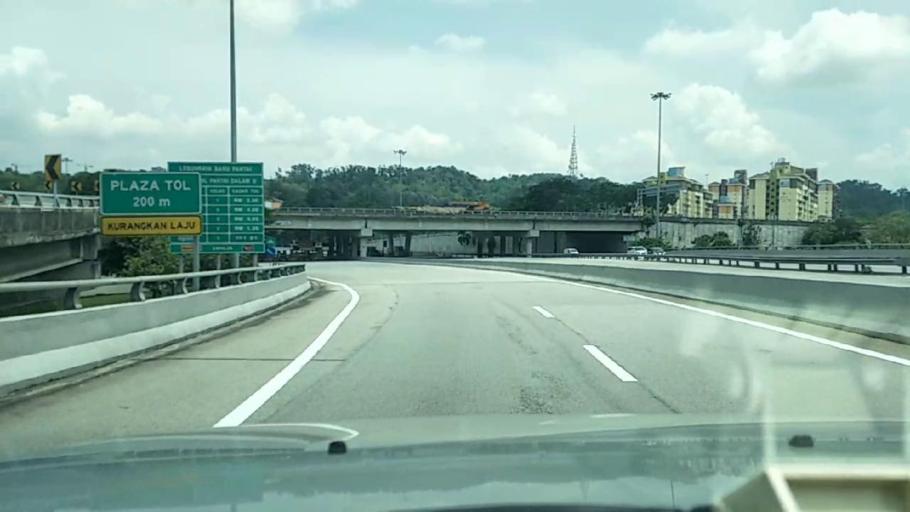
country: MY
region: Kuala Lumpur
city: Kuala Lumpur
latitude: 3.0940
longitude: 101.6721
